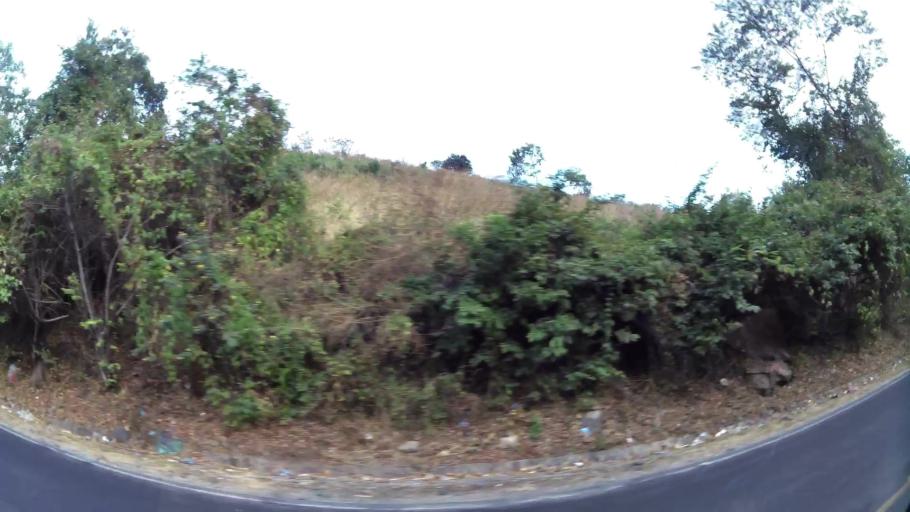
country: SV
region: San Vicente
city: Apastepeque
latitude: 13.6568
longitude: -88.7908
